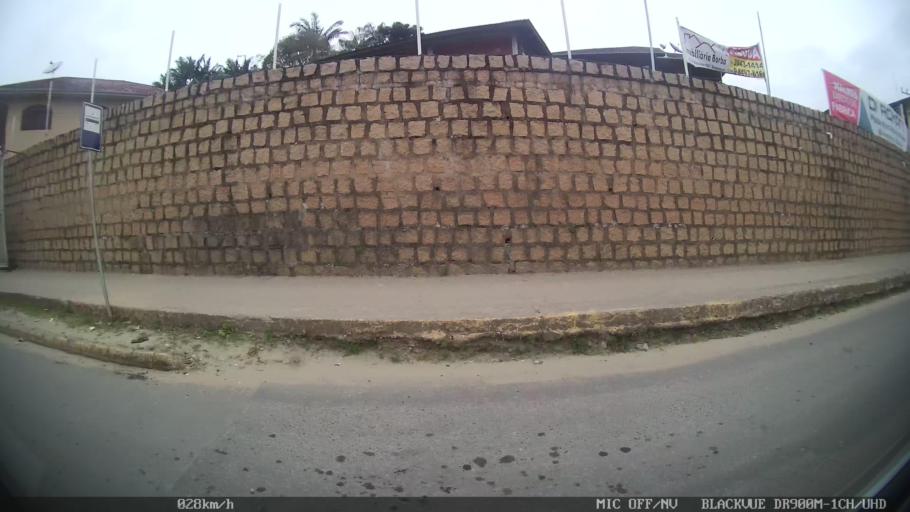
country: BR
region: Santa Catarina
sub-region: Joinville
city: Joinville
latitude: -26.3610
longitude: -48.8344
